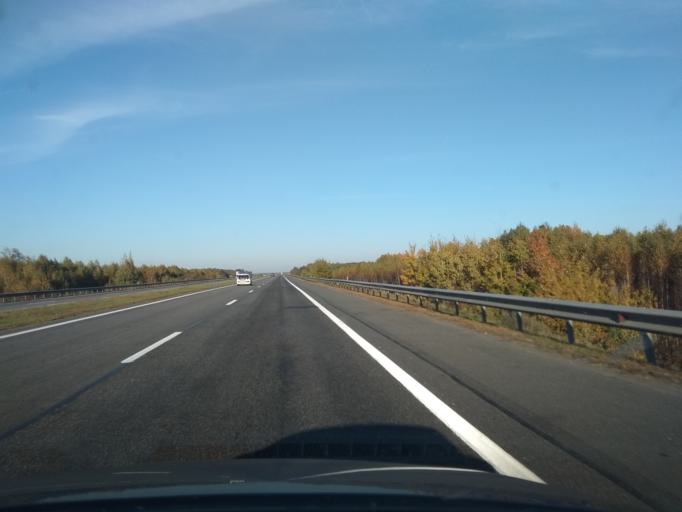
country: BY
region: Brest
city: Nyakhachava
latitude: 52.5945
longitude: 25.1476
